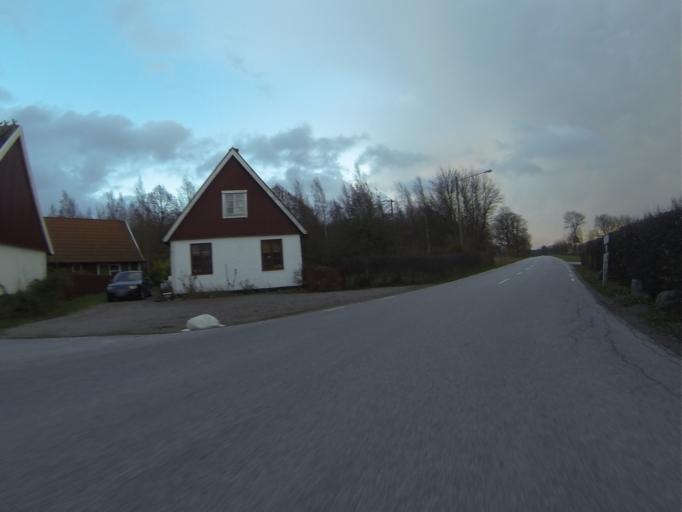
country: SE
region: Skane
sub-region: Lunds Kommun
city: Genarp
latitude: 55.6212
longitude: 13.4059
